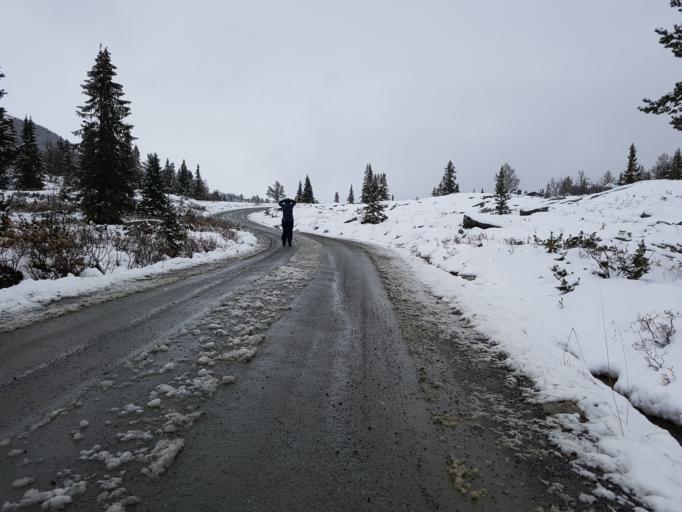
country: NO
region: Oppland
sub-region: Sel
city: Otta
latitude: 61.8058
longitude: 9.6898
